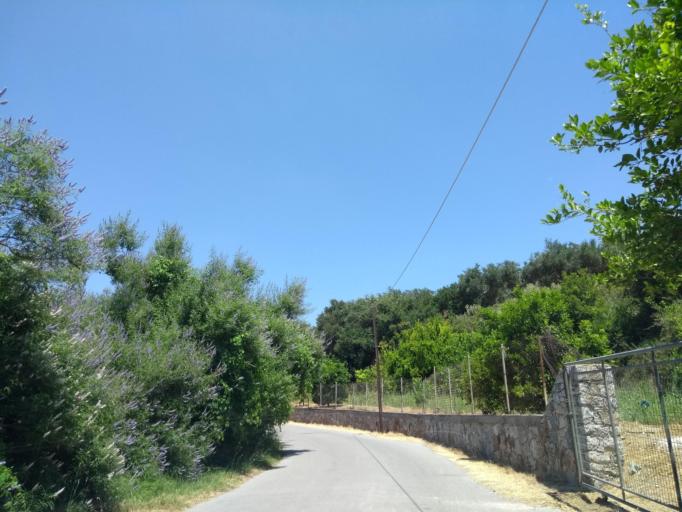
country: GR
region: Crete
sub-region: Nomos Chanias
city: Georgioupolis
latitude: 35.3337
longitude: 24.2781
